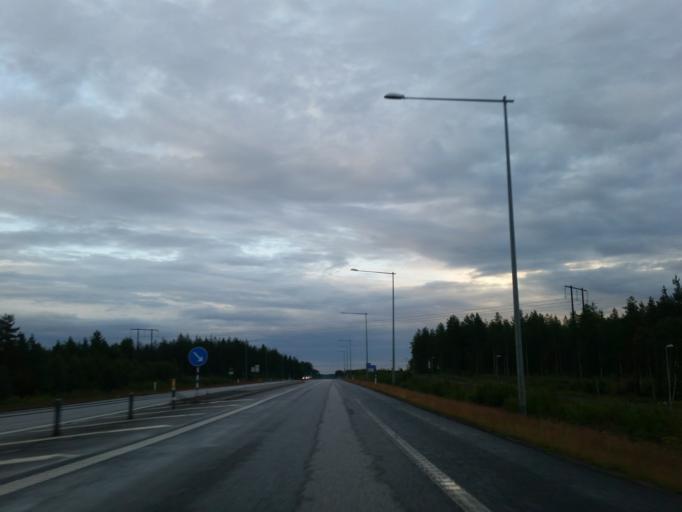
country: SE
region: Vaesterbotten
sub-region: Umea Kommun
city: Taftea
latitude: 63.8604
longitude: 20.4083
